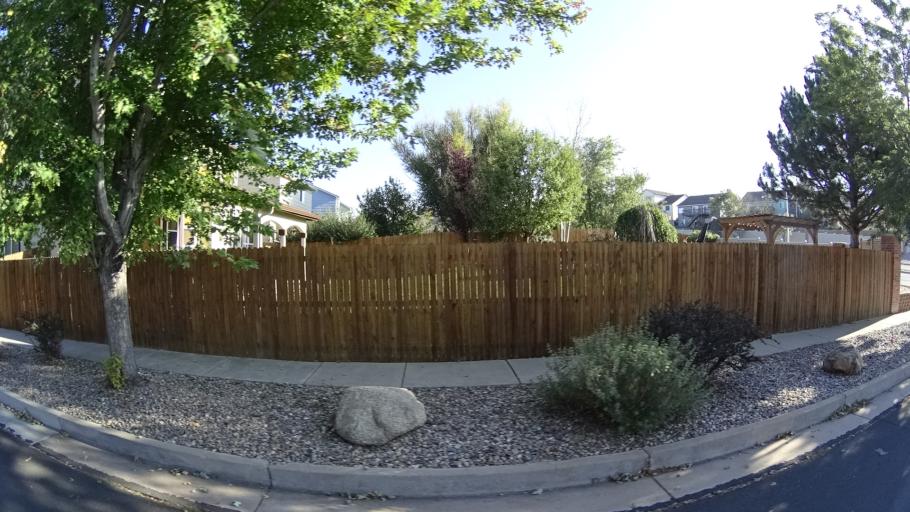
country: US
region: Colorado
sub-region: El Paso County
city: Cimarron Hills
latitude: 38.8905
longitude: -104.7025
